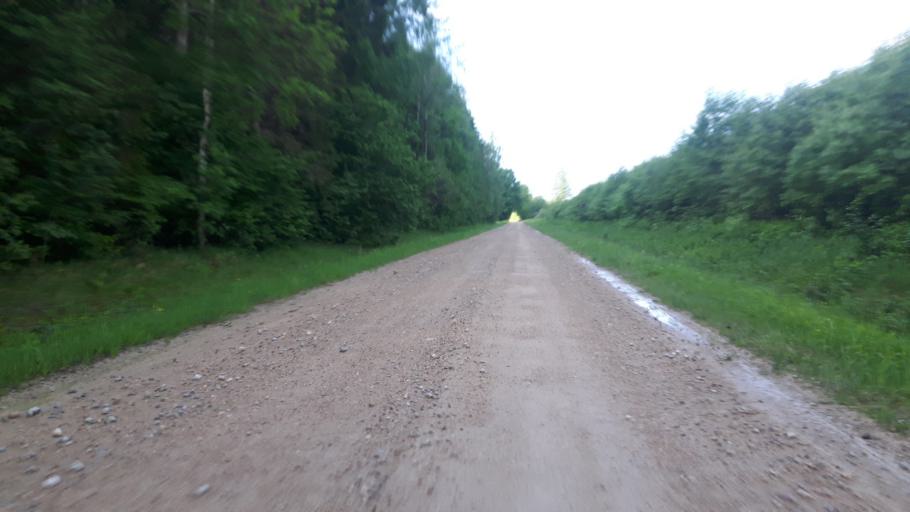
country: EE
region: Paernumaa
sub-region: Vaendra vald (alev)
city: Vandra
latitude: 58.7089
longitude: 25.0424
